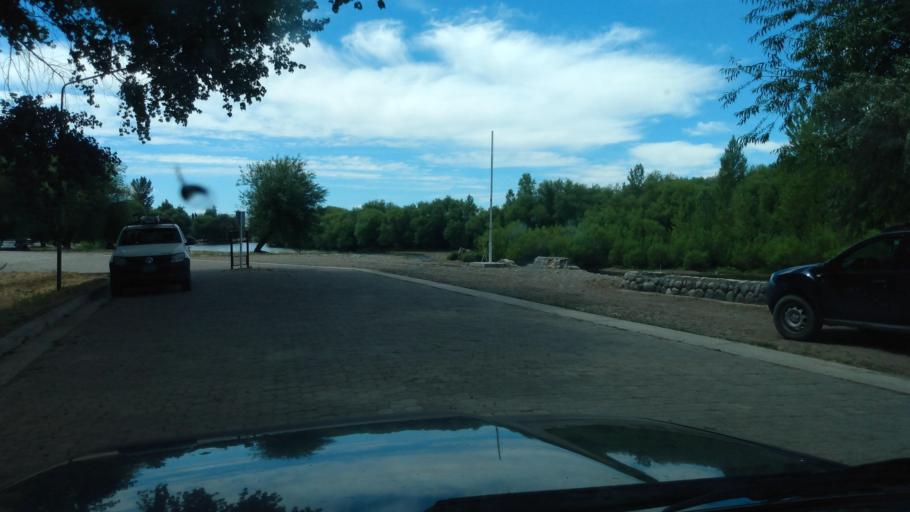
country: AR
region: Neuquen
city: Junin de los Andes
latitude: -39.9465
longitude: -71.0647
